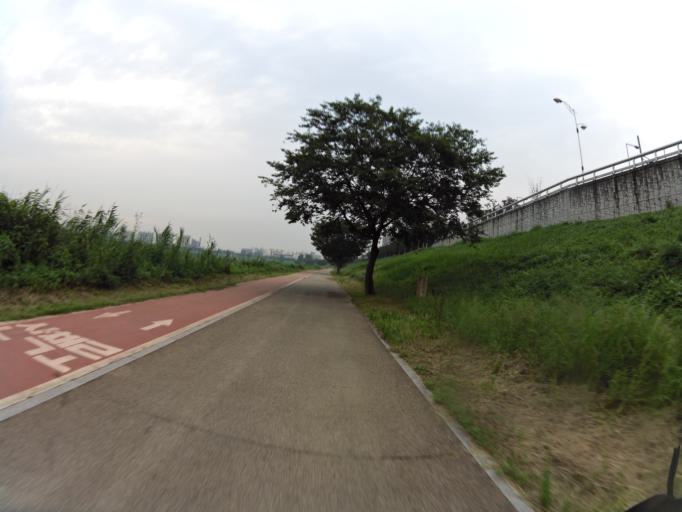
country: KR
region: Gyeongsangbuk-do
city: Gyeongsan-si
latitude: 35.8705
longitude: 128.6802
